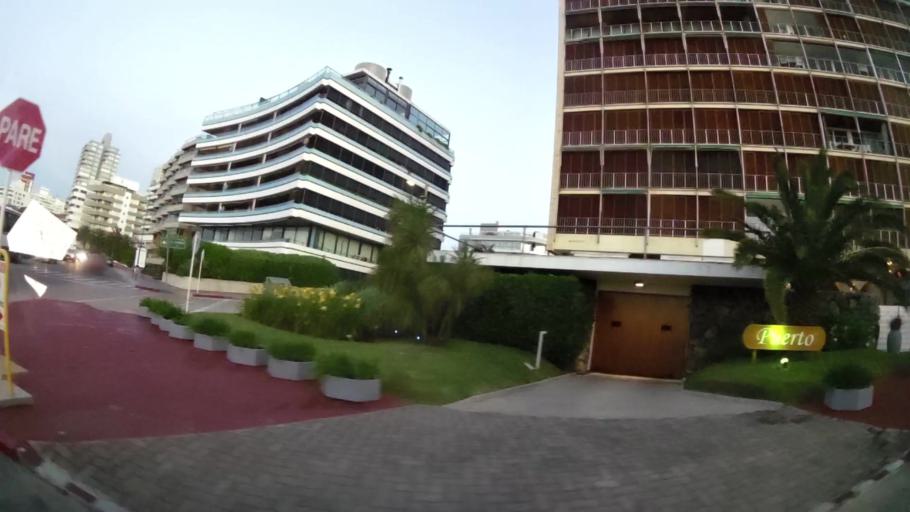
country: UY
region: Maldonado
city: Punta del Este
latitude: -34.9651
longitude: -54.9481
